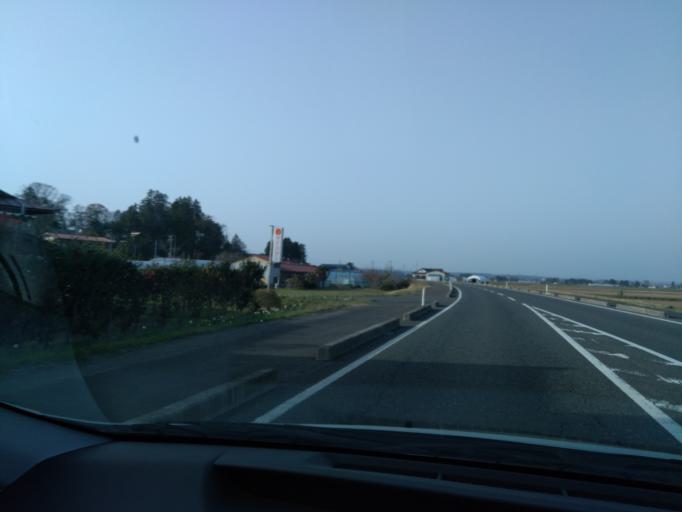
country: JP
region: Iwate
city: Ichinoseki
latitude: 38.7407
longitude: 141.1306
